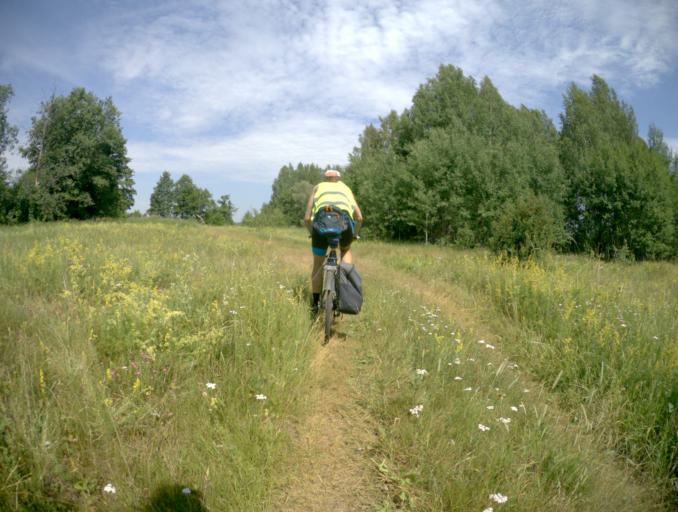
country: RU
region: Vladimir
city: Vorsha
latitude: 56.0288
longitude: 40.1833
